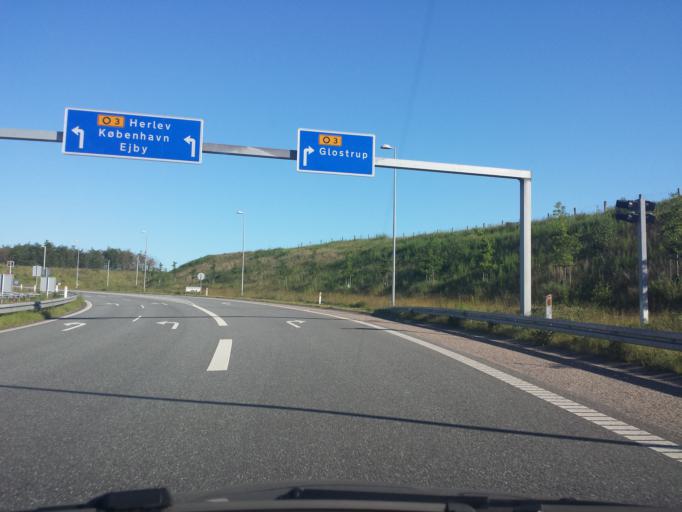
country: DK
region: Capital Region
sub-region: Glostrup Kommune
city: Glostrup
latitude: 55.6916
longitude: 12.4035
